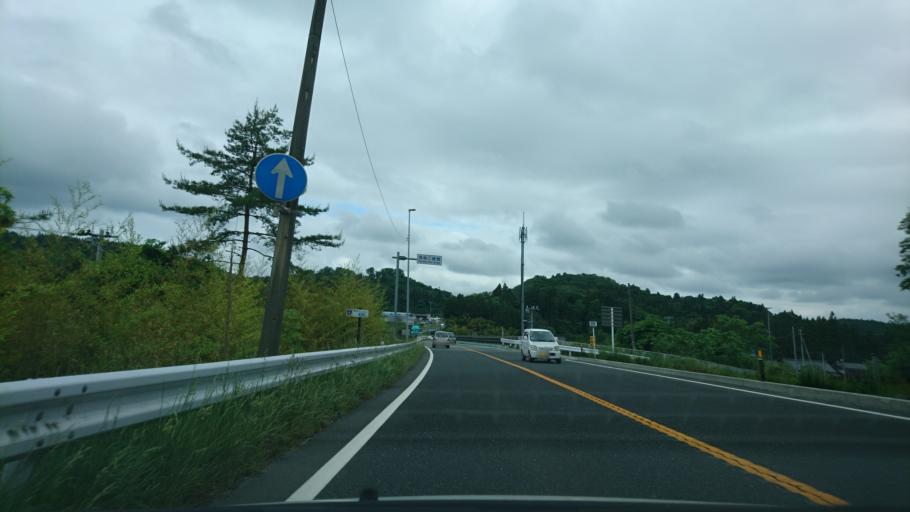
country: JP
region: Iwate
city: Ichinoseki
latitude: 38.8880
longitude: 141.1179
